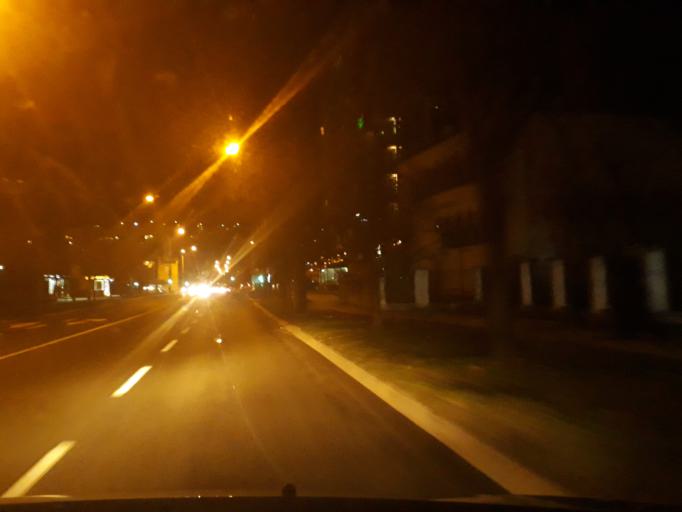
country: BA
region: Federation of Bosnia and Herzegovina
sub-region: Kanton Sarajevo
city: Sarajevo
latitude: 43.8495
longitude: 18.3798
